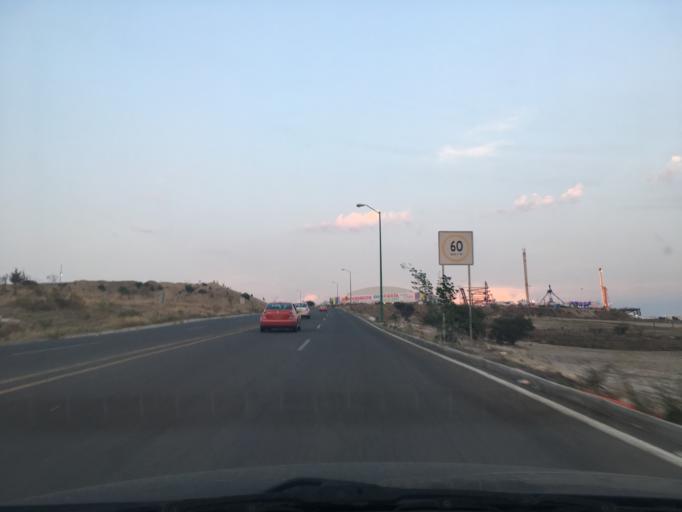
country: MX
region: Michoacan
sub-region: Morelia
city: La Aldea
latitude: 19.7299
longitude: -101.0945
